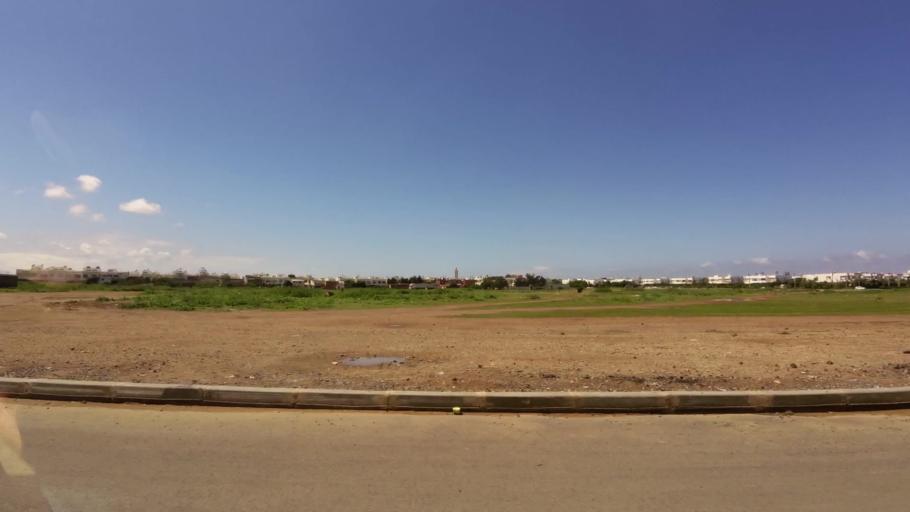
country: MA
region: Grand Casablanca
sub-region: Nouaceur
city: Dar Bouazza
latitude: 33.5192
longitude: -7.8189
